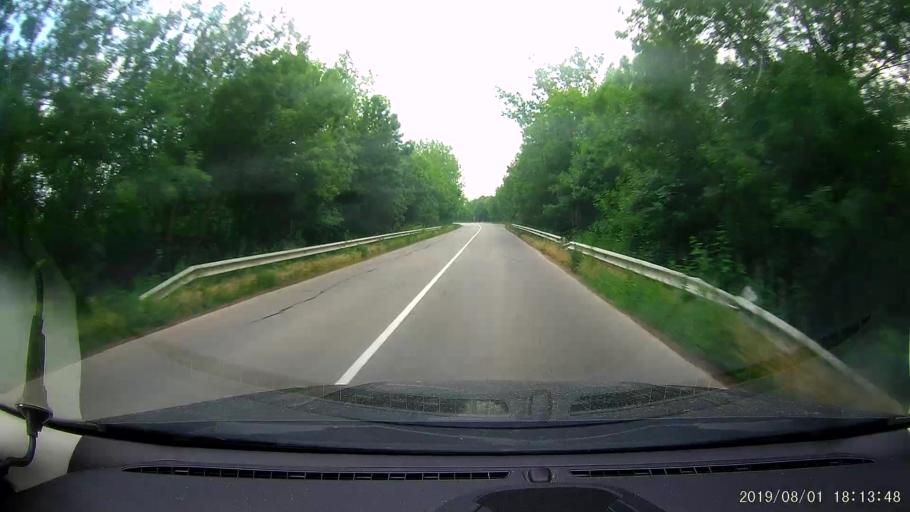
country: BG
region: Silistra
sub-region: Obshtina Dulovo
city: Dulovo
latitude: 43.7822
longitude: 27.1322
